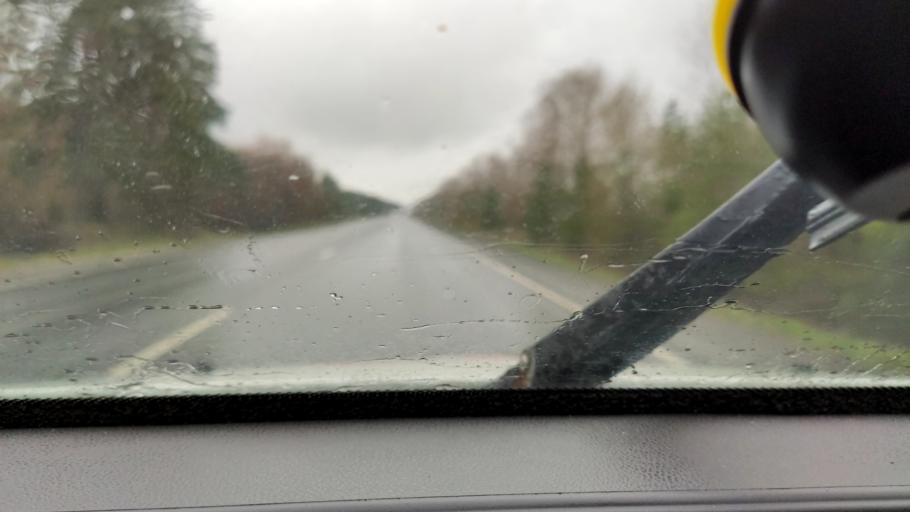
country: RU
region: Samara
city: Povolzhskiy
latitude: 53.6199
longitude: 49.6387
